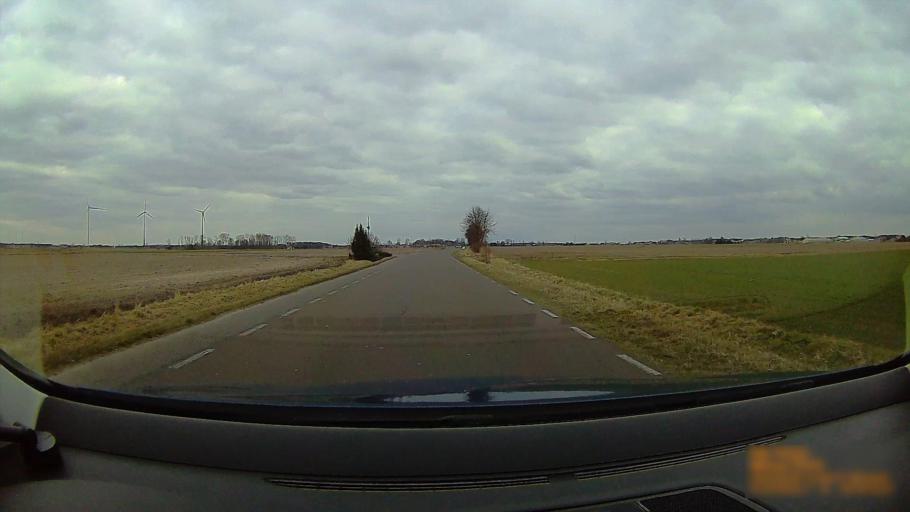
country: PL
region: Greater Poland Voivodeship
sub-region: Powiat koninski
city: Rychwal
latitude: 52.0974
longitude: 18.1209
